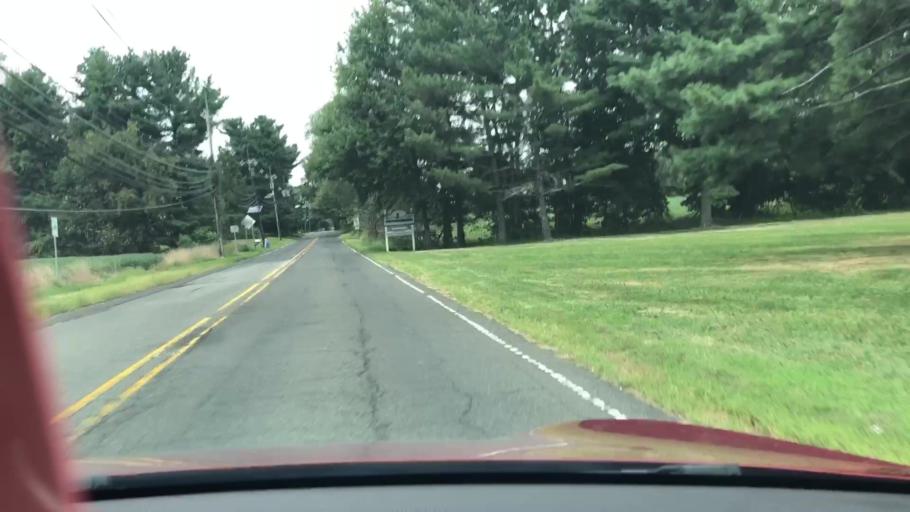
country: US
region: New Jersey
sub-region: Monmouth County
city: Allentown
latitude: 40.1820
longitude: -74.5901
